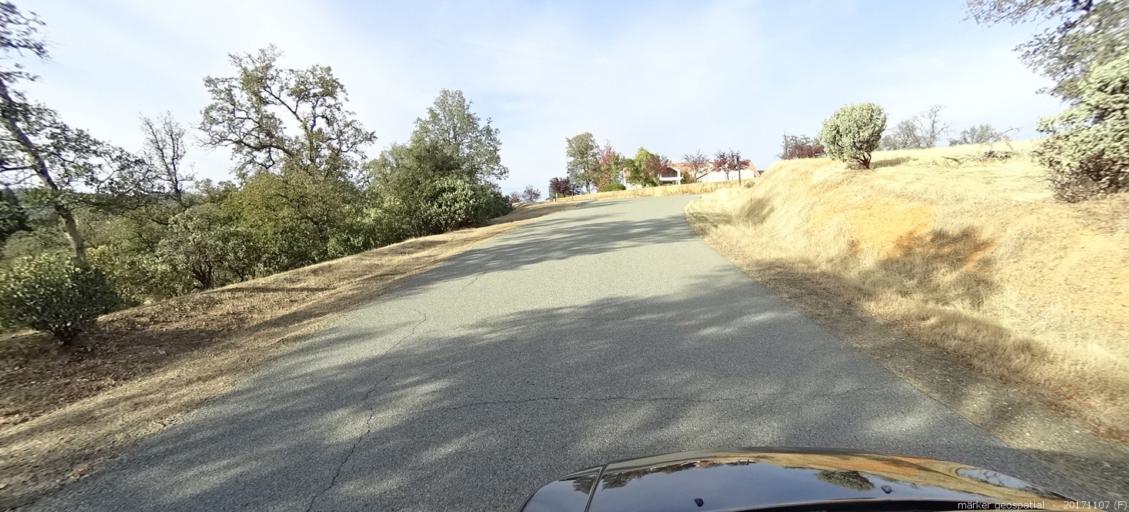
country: US
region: California
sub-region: Shasta County
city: Shasta
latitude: 40.5068
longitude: -122.4724
